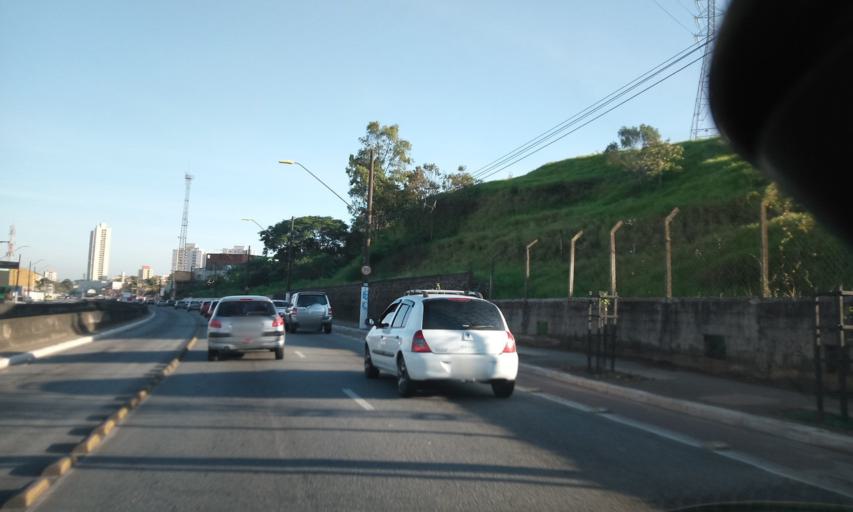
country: BR
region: Sao Paulo
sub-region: Santo Andre
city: Santo Andre
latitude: -23.6805
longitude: -46.5052
